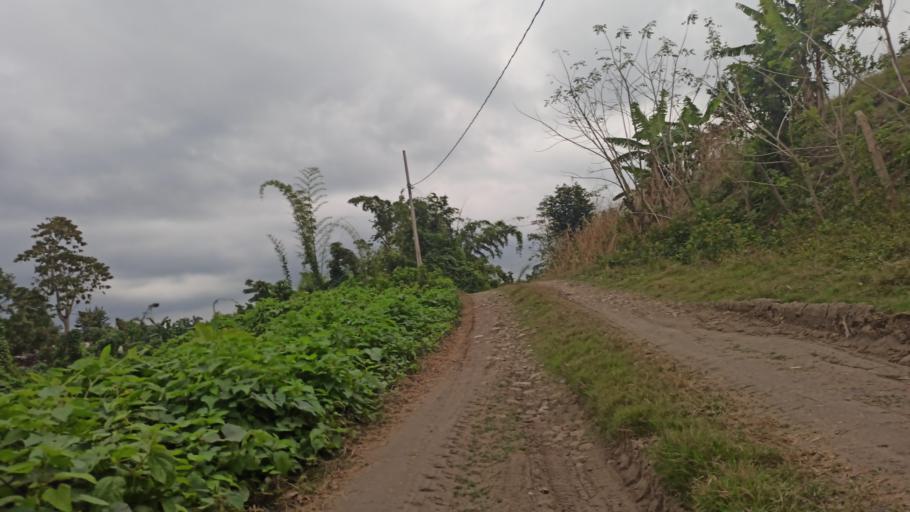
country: MX
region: Veracruz
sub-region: Papantla
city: El Chote
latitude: 20.3645
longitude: -97.4311
